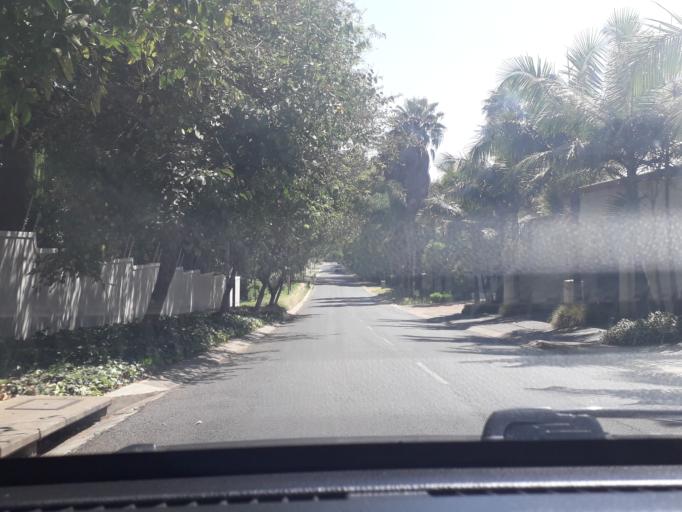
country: ZA
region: Gauteng
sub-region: City of Johannesburg Metropolitan Municipality
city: Modderfontein
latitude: -26.0973
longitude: 28.0710
